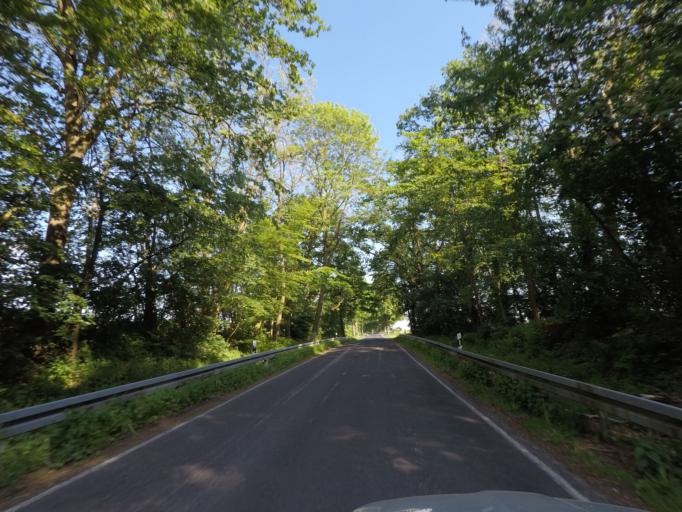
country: DE
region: Brandenburg
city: Hohenfinow
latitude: 52.7233
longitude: 13.8925
